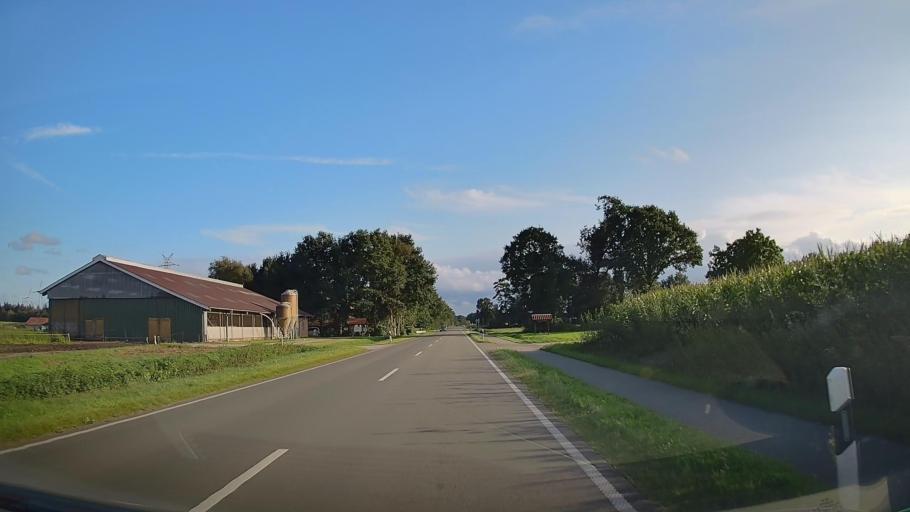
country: DE
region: Lower Saxony
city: Barssel
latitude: 53.1028
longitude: 7.7096
